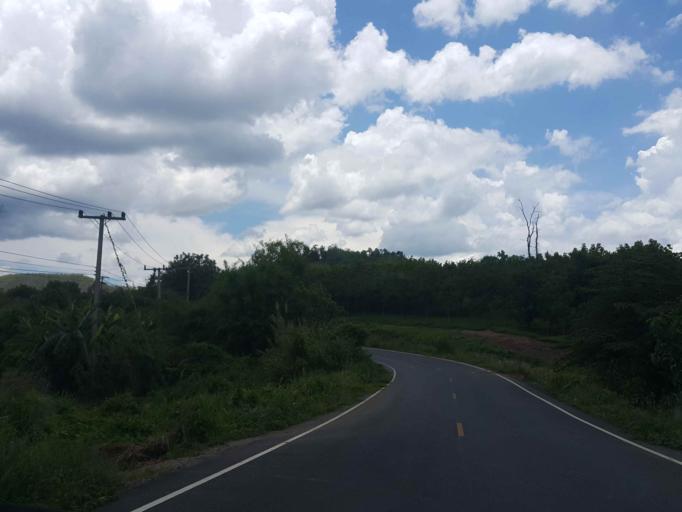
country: TH
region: Nan
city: Wiang Sa
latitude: 18.5365
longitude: 100.5490
